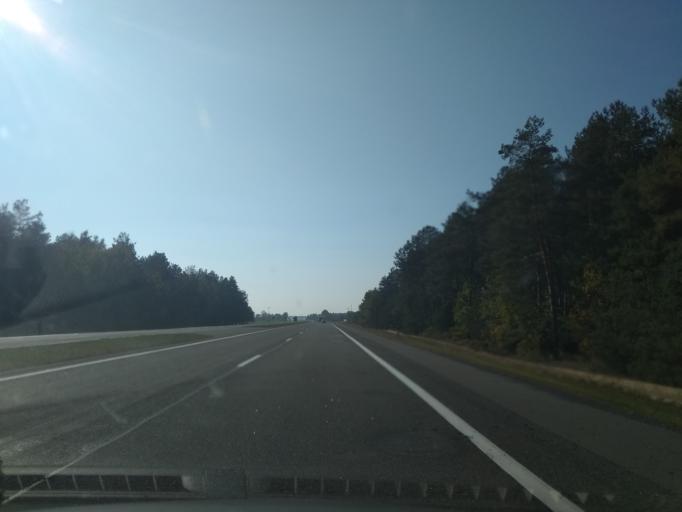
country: BY
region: Brest
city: Antopal'
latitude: 52.3382
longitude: 24.6458
